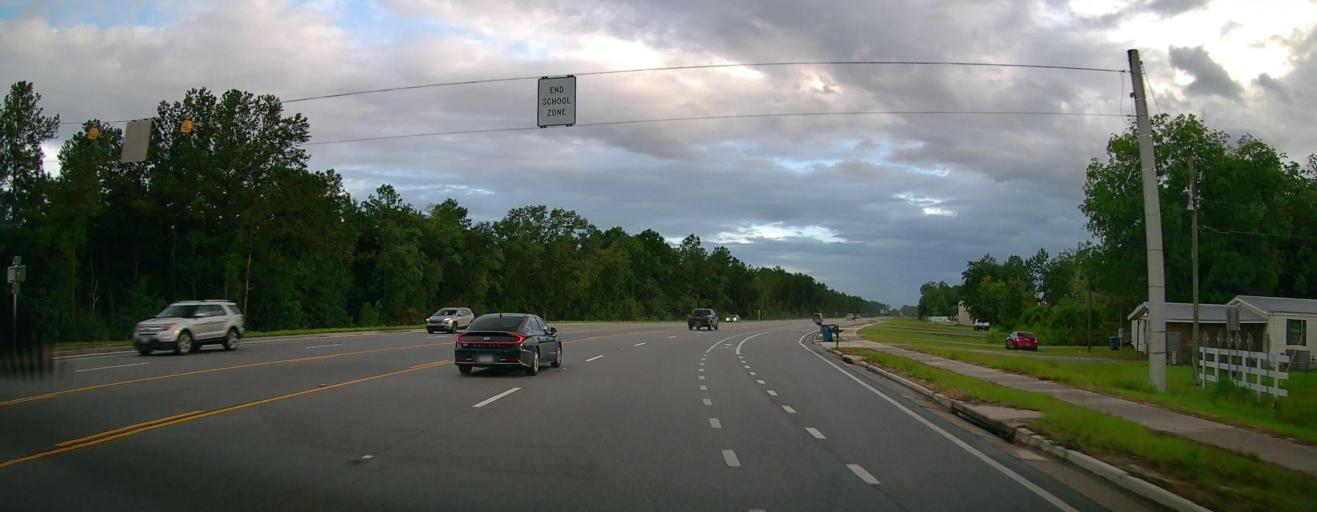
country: US
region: Georgia
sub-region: Ware County
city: Deenwood
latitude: 31.1924
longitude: -82.3841
